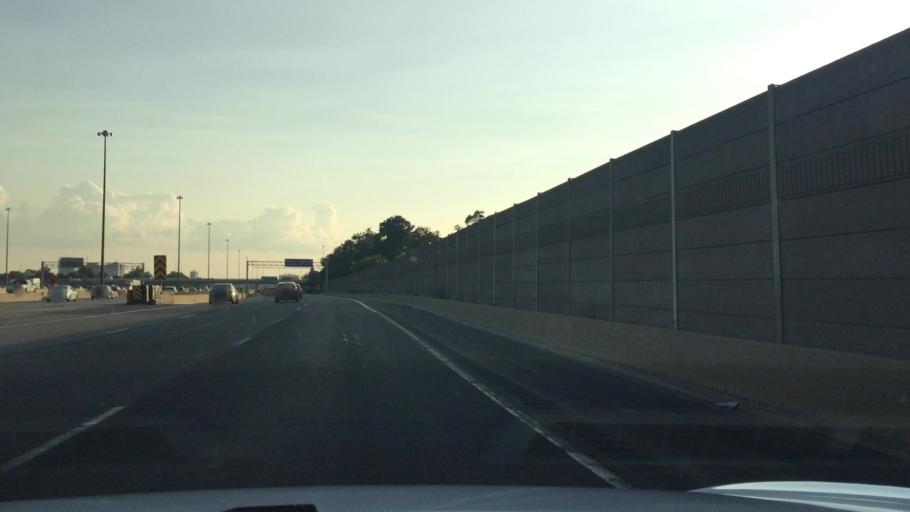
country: CA
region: Ontario
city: Scarborough
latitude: 43.7732
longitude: -79.2990
